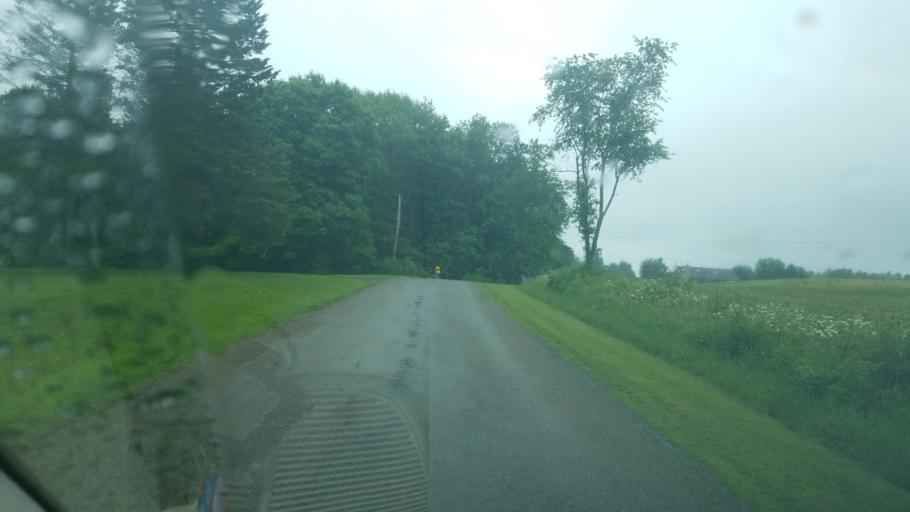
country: US
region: Ohio
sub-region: Sandusky County
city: Bellville
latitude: 40.6353
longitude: -82.4150
